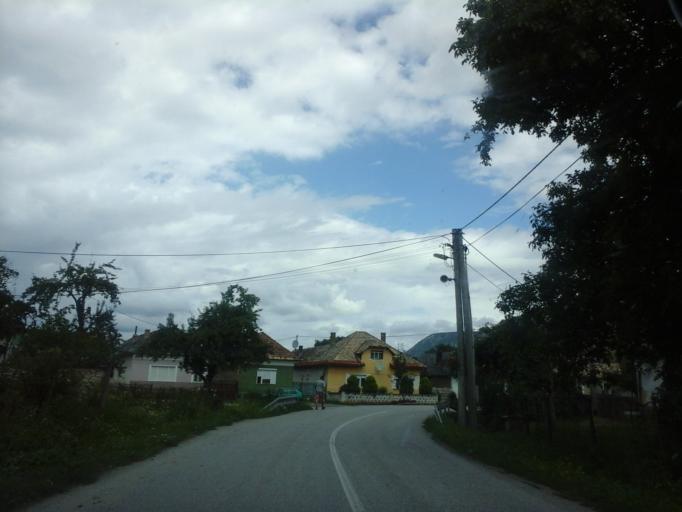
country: SK
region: Kosicky
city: Roznava
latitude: 48.5908
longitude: 20.3823
